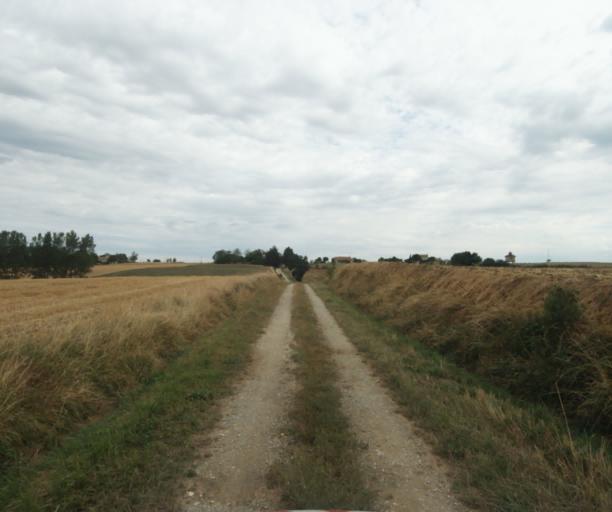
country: FR
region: Midi-Pyrenees
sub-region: Departement de la Haute-Garonne
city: Revel
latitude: 43.4327
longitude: 1.9591
